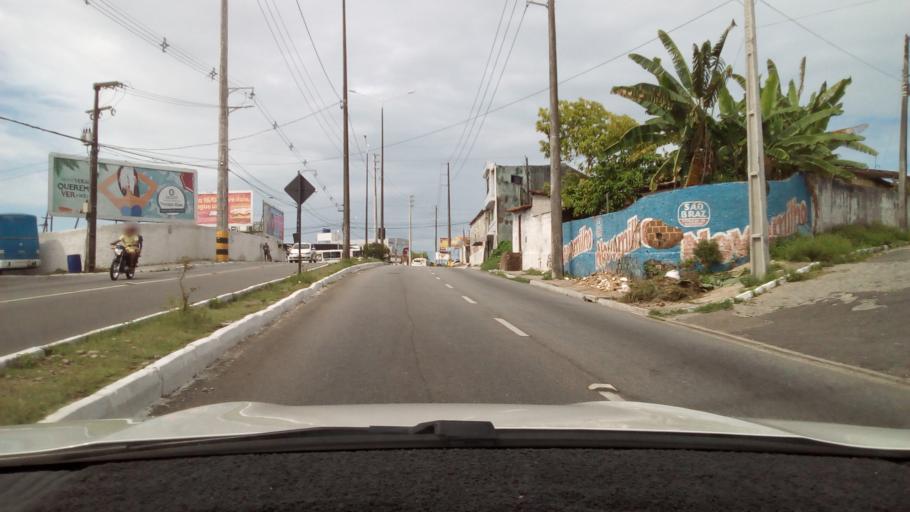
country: BR
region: Paraiba
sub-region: Joao Pessoa
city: Joao Pessoa
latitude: -7.1042
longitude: -34.8646
